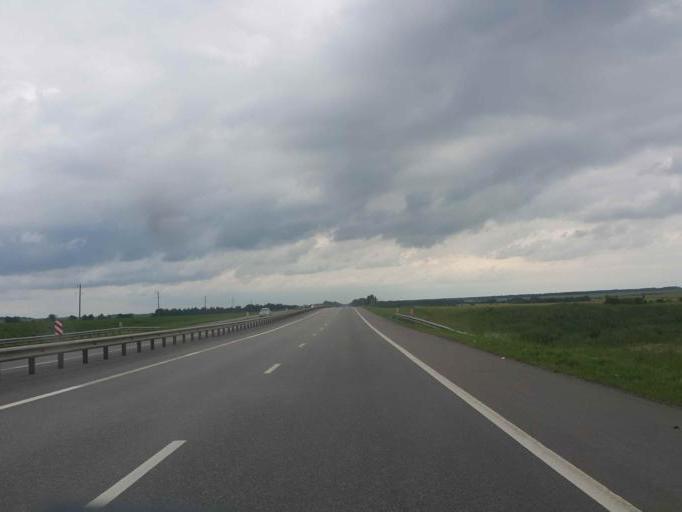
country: RU
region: Tambov
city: Selezni
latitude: 52.8195
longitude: 40.9290
